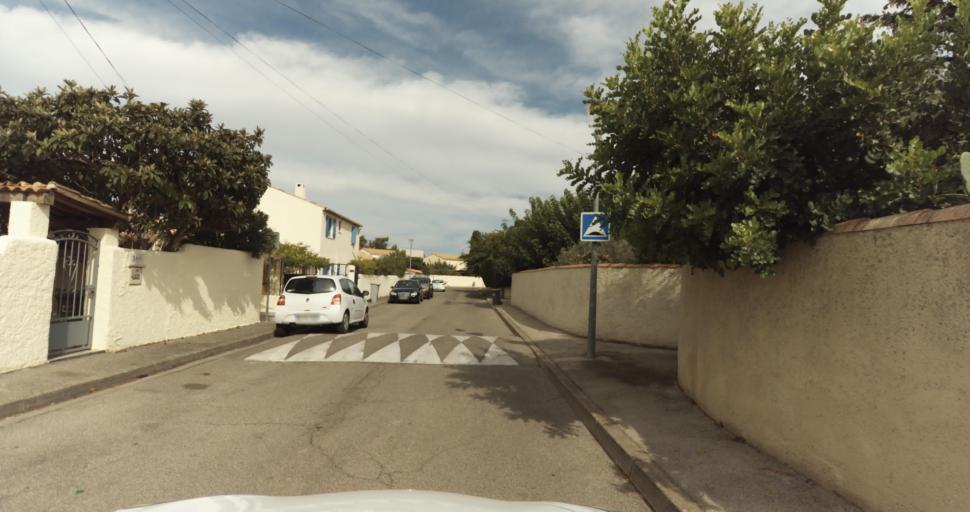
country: FR
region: Provence-Alpes-Cote d'Azur
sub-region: Departement des Bouches-du-Rhone
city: Miramas
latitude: 43.5959
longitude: 5.0029
